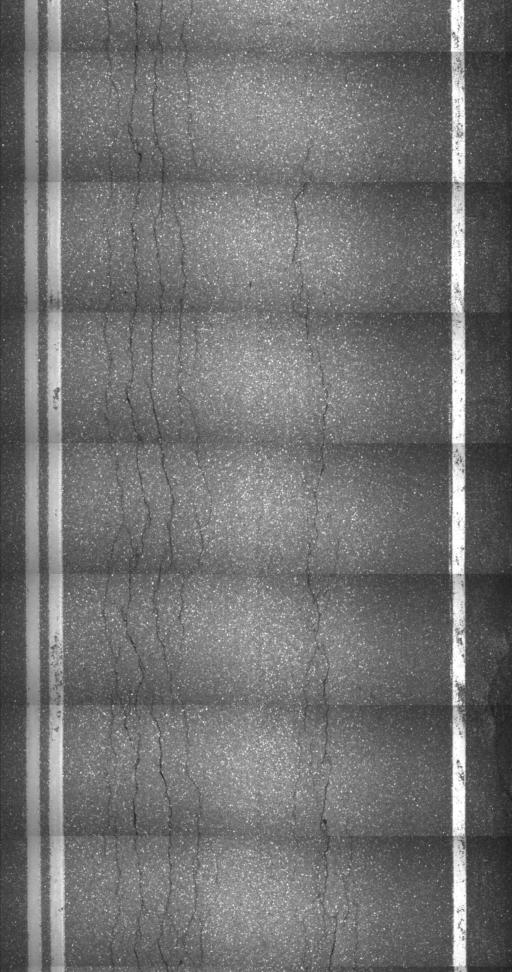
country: US
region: Vermont
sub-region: Caledonia County
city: Lyndonville
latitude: 44.6418
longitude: -72.1542
